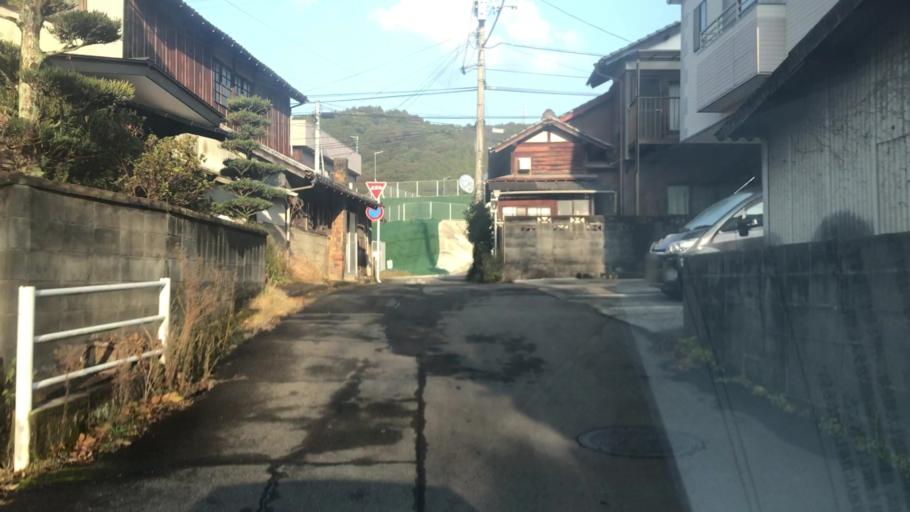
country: JP
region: Saga Prefecture
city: Takeocho-takeo
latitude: 33.1975
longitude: 130.0190
